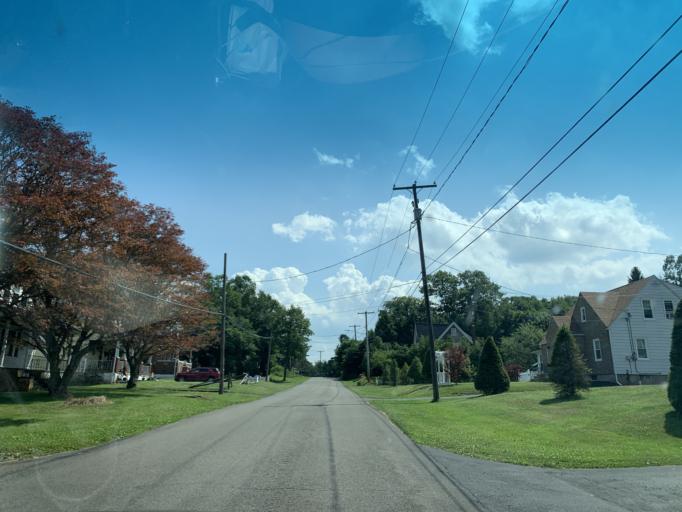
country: US
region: Pennsylvania
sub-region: Schuylkill County
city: Ashland
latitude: 40.8136
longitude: -76.3386
